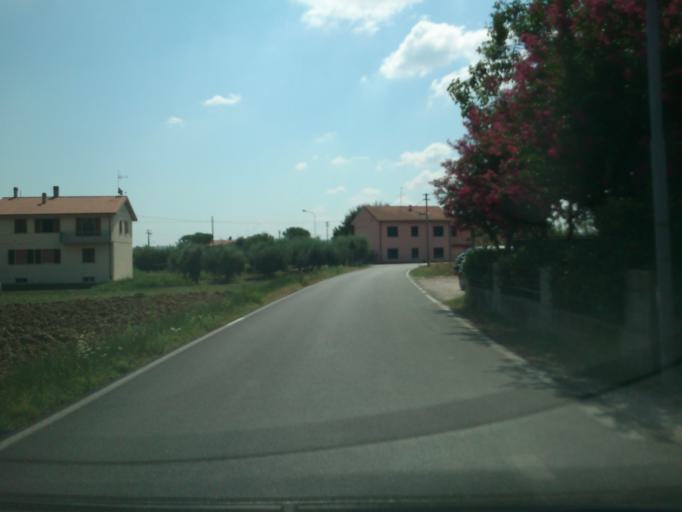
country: IT
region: The Marches
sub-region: Provincia di Pesaro e Urbino
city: Bellocchi
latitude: 43.7997
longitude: 12.9863
